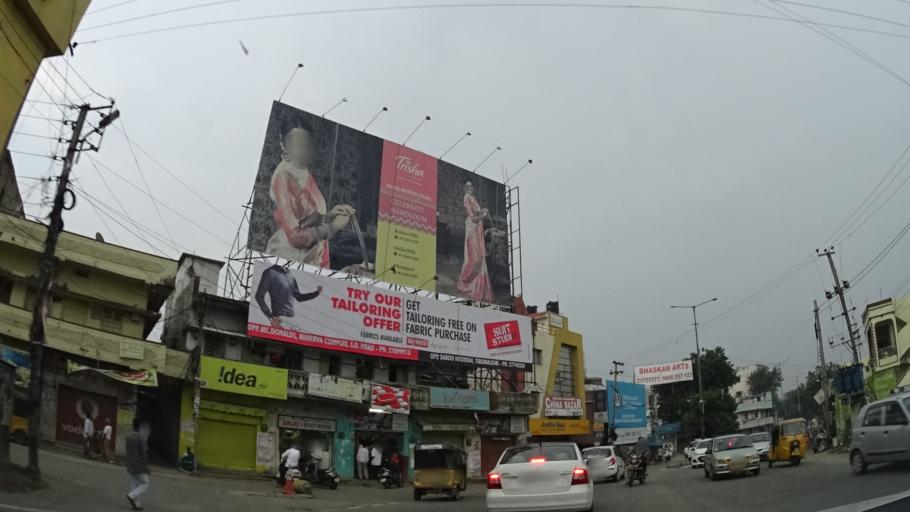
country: IN
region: Telangana
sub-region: Rangareddi
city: Quthbullapur
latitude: 17.4616
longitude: 78.4756
